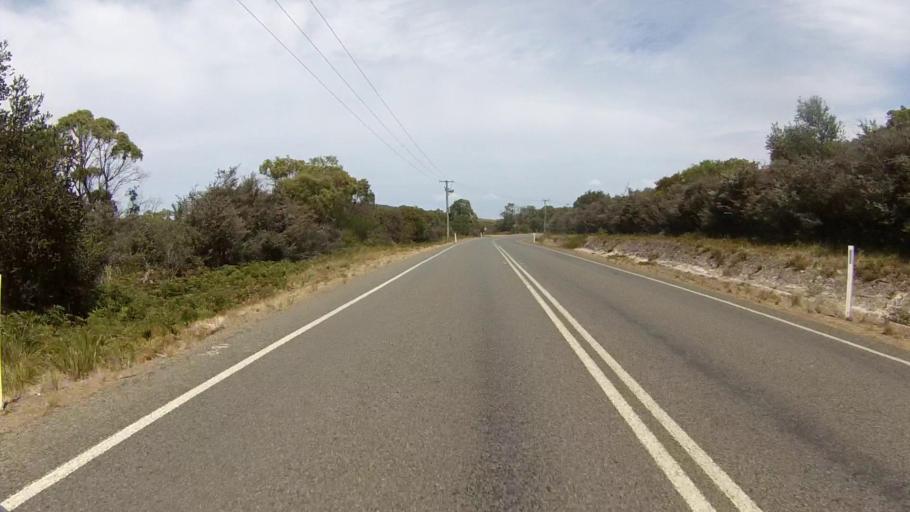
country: AU
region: Tasmania
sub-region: Clarence
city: Sandford
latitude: -43.0224
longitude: 147.4875
